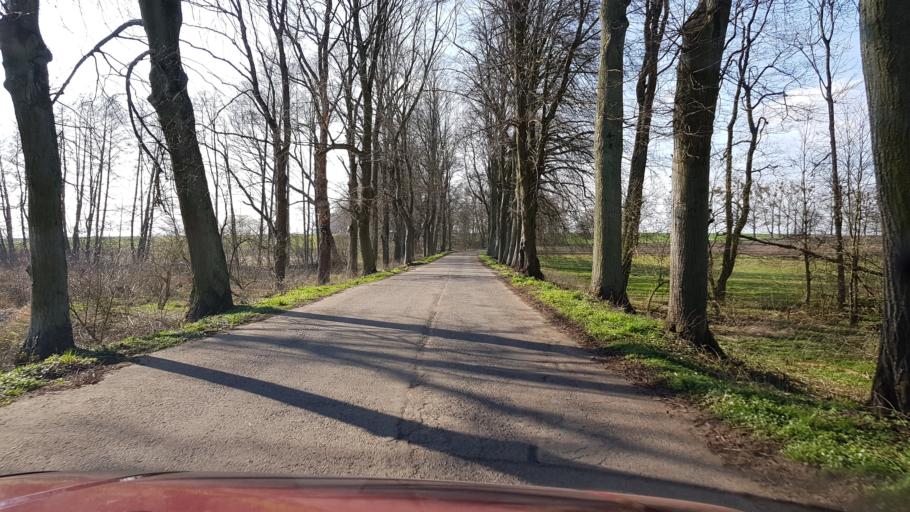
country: PL
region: West Pomeranian Voivodeship
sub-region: Powiat gryficki
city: Ploty
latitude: 53.7095
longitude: 15.2671
